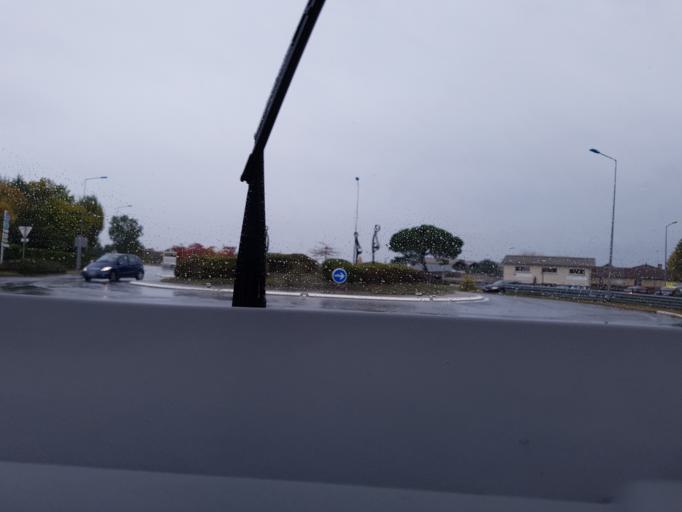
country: FR
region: Aquitaine
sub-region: Departement de la Gironde
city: Cubzac-les-Ponts
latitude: 44.9930
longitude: -0.4337
